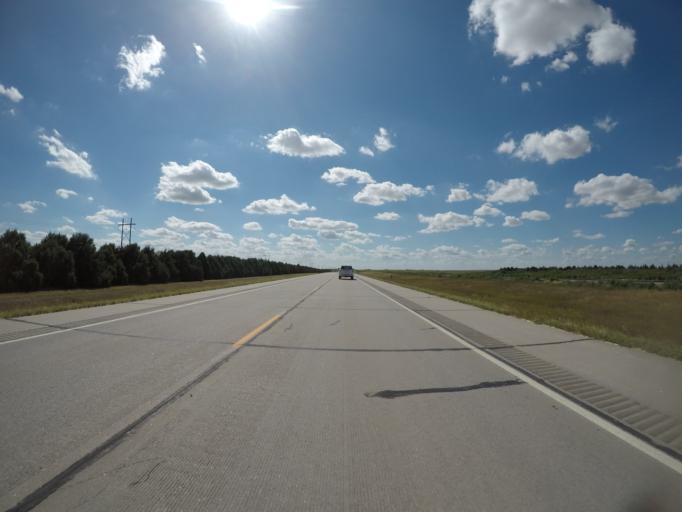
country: US
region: Colorado
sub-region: Phillips County
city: Holyoke
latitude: 40.5988
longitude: -102.3908
